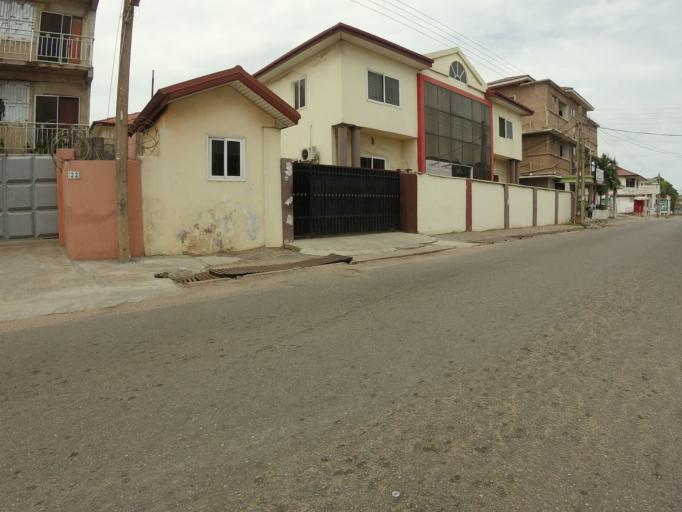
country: GH
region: Greater Accra
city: Accra
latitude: 5.5769
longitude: -0.2094
